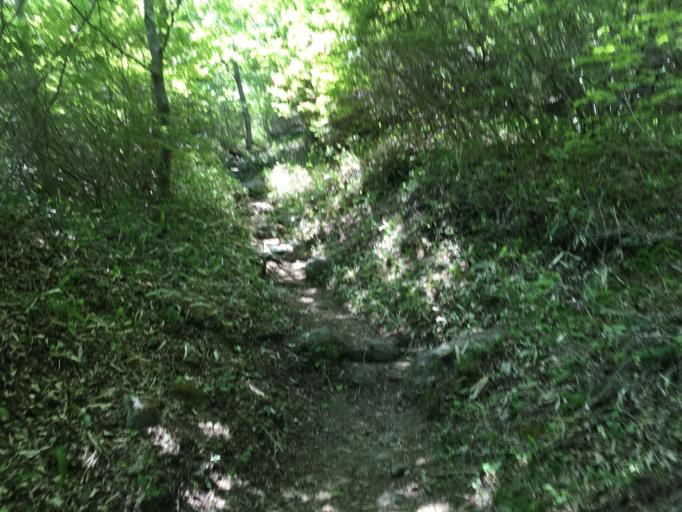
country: JP
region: Iwate
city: Ofunato
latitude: 39.1802
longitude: 141.7409
